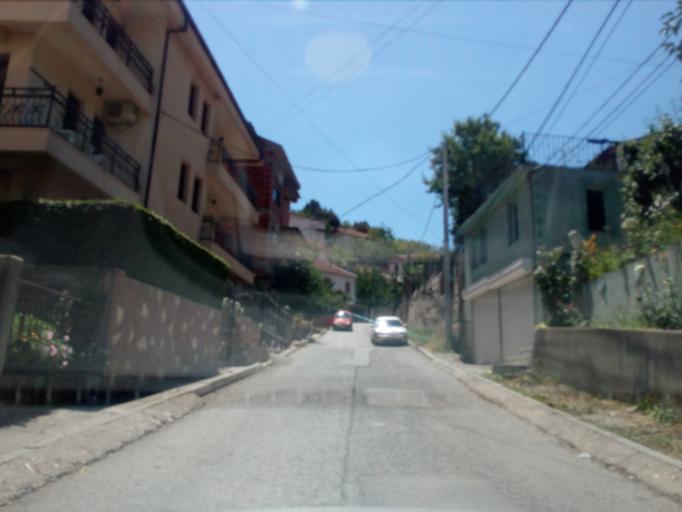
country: MK
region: Veles
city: Veles
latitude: 41.7140
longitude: 21.7745
